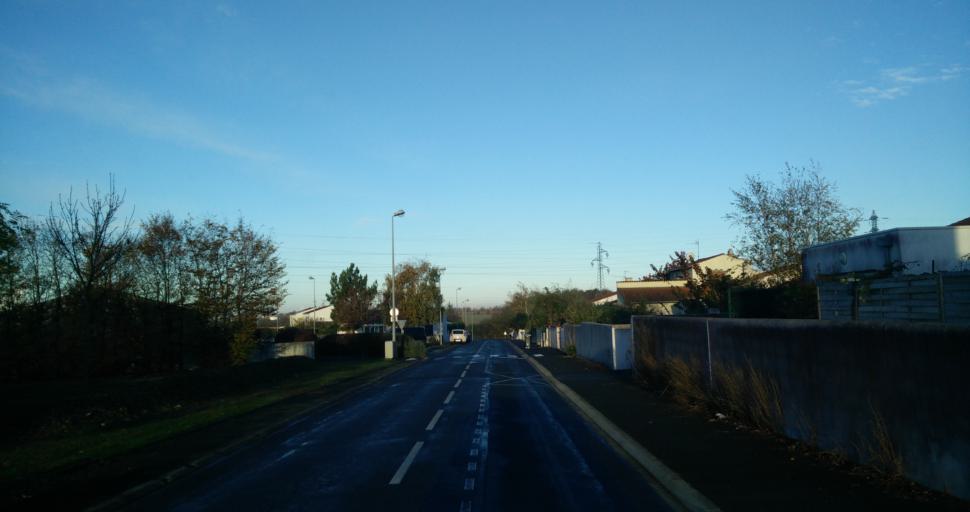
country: FR
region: Poitou-Charentes
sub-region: Departement de la Charente-Maritime
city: Puilboreau
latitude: 46.1864
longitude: -1.1215
